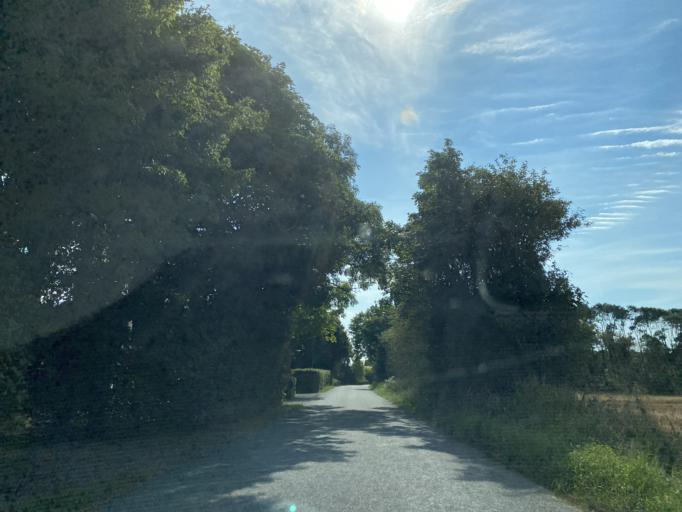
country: DK
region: Central Jutland
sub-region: Viborg Kommune
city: Bjerringbro
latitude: 56.3459
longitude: 9.7211
